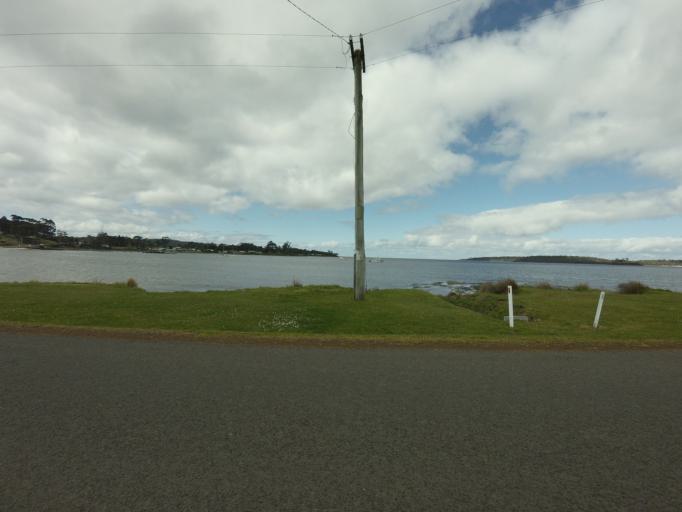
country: AU
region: Tasmania
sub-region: Huon Valley
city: Geeveston
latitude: -43.4331
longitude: 146.9689
